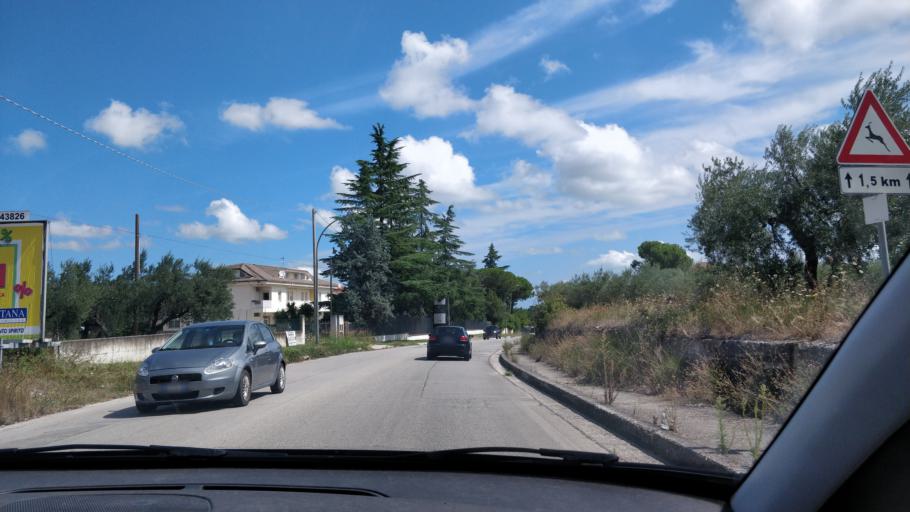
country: IT
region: Abruzzo
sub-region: Provincia di Chieti
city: Treglio
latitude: 42.2442
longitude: 14.4147
